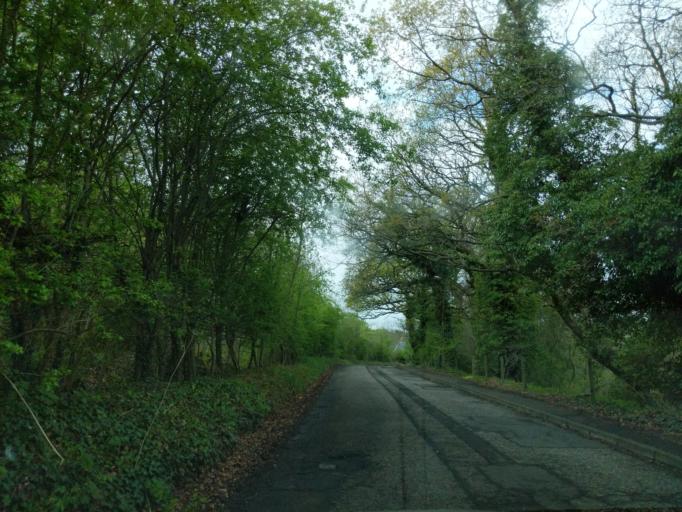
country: GB
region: Scotland
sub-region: Edinburgh
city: Currie
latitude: 55.8979
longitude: -3.2958
